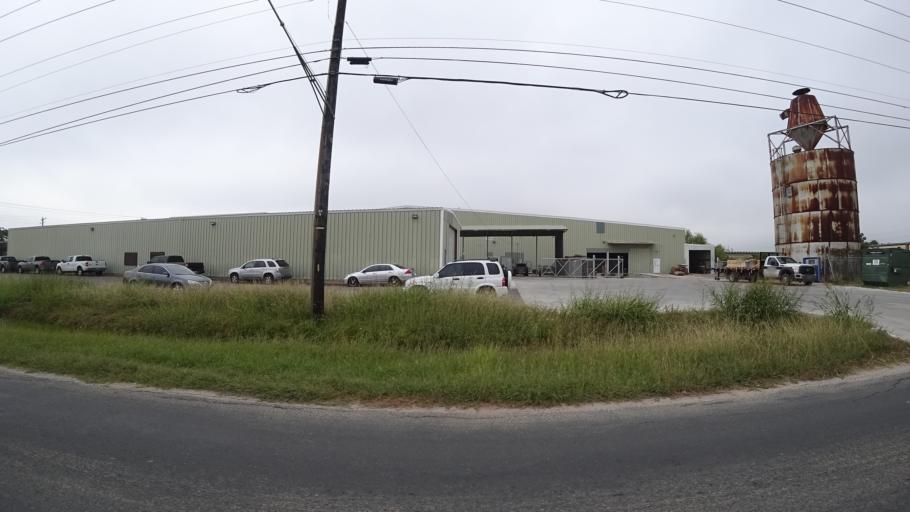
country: US
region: Texas
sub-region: Travis County
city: Austin
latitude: 30.2175
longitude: -97.7578
